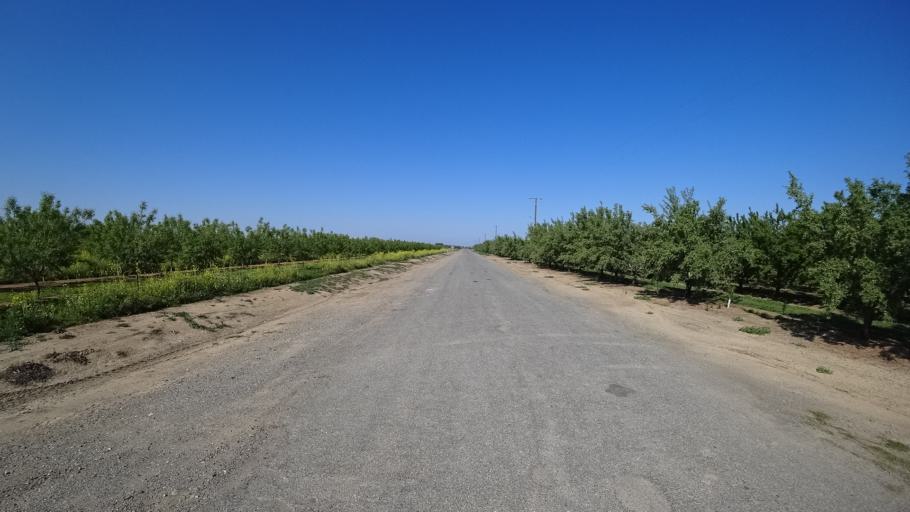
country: US
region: California
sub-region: Glenn County
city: Hamilton City
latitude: 39.6377
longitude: -122.0078
